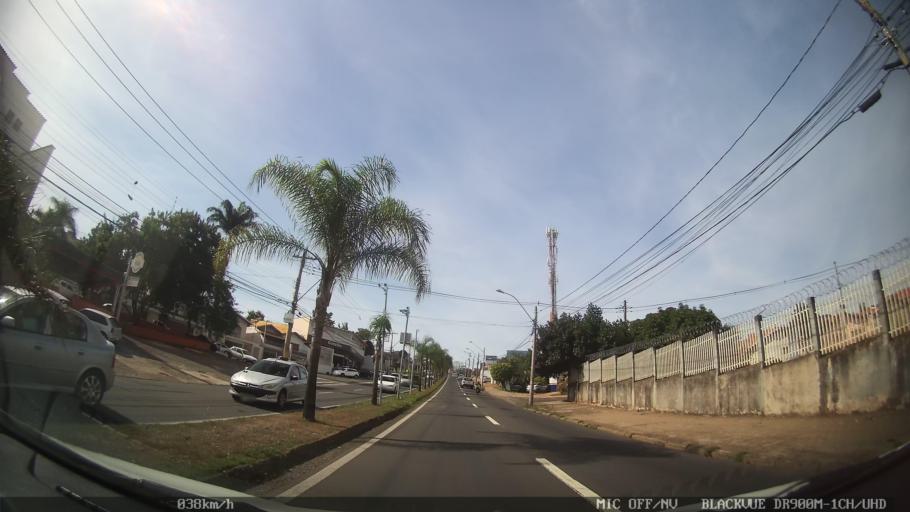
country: BR
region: Sao Paulo
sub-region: Piracicaba
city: Piracicaba
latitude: -22.7325
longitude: -47.6617
